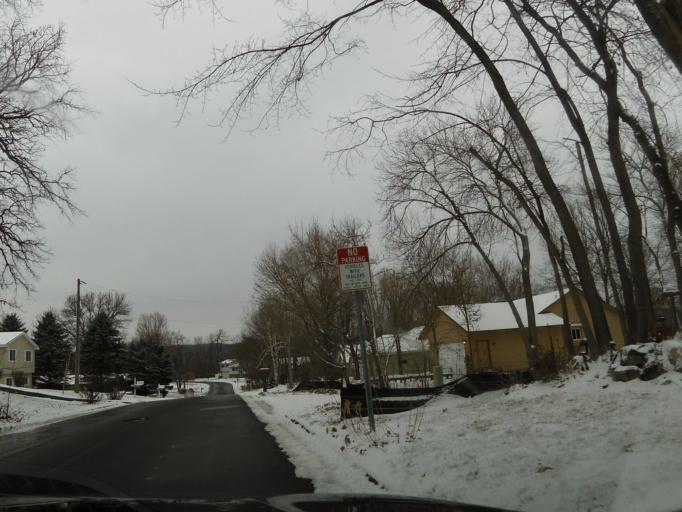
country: US
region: Minnesota
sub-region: Scott County
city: Prior Lake
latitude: 44.7060
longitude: -93.4611
